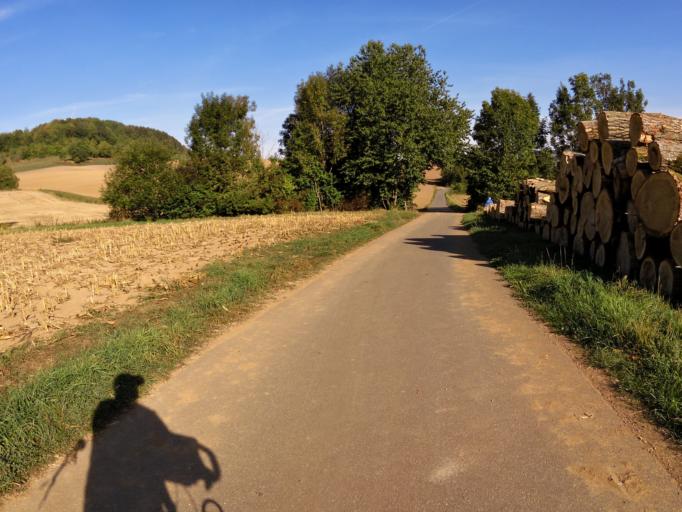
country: DE
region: Rheinland-Pfalz
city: Nusbaum
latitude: 49.9269
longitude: 6.3541
